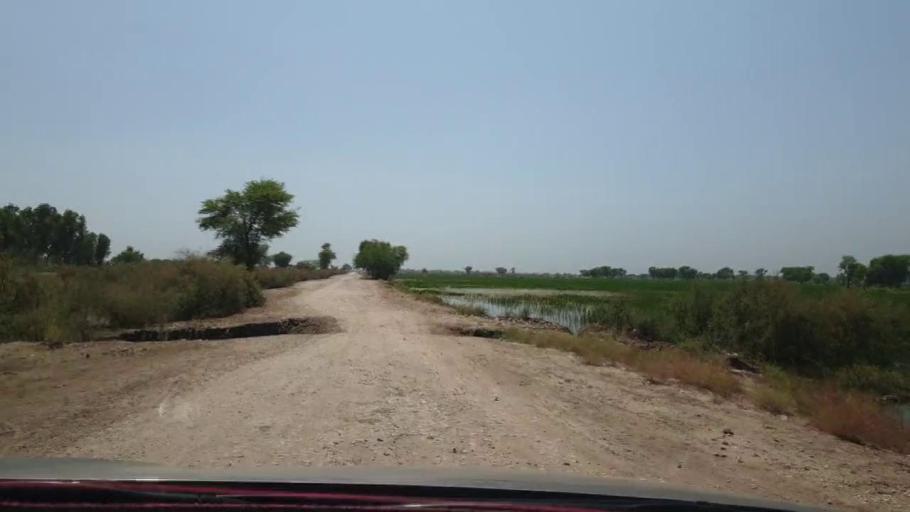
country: PK
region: Sindh
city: Kambar
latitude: 27.5702
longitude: 67.8806
